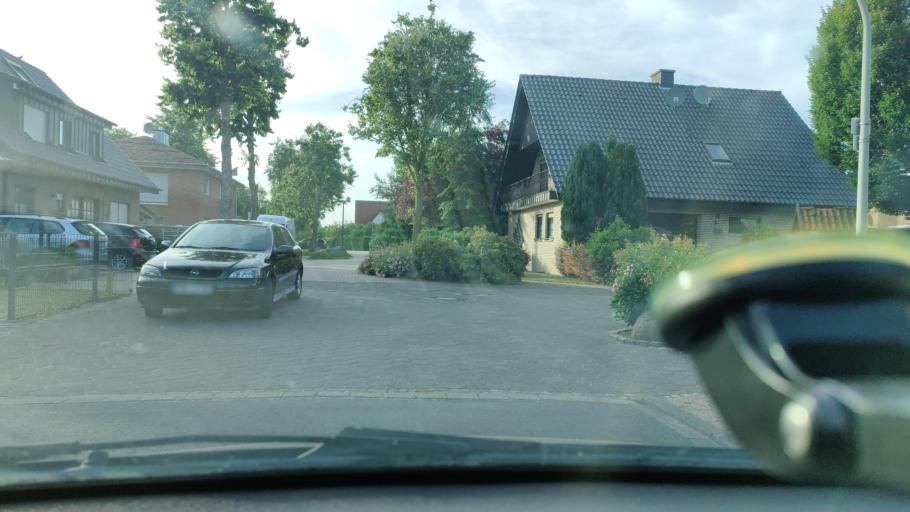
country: DE
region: North Rhine-Westphalia
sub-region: Regierungsbezirk Munster
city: Coesfeld
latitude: 52.0189
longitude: 7.2041
